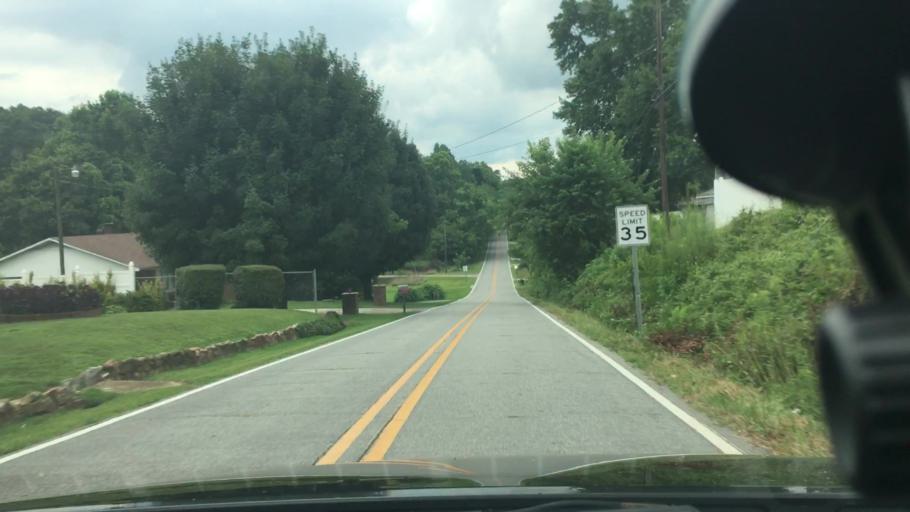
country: US
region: North Carolina
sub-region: McDowell County
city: West Marion
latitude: 35.6617
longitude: -82.0172
